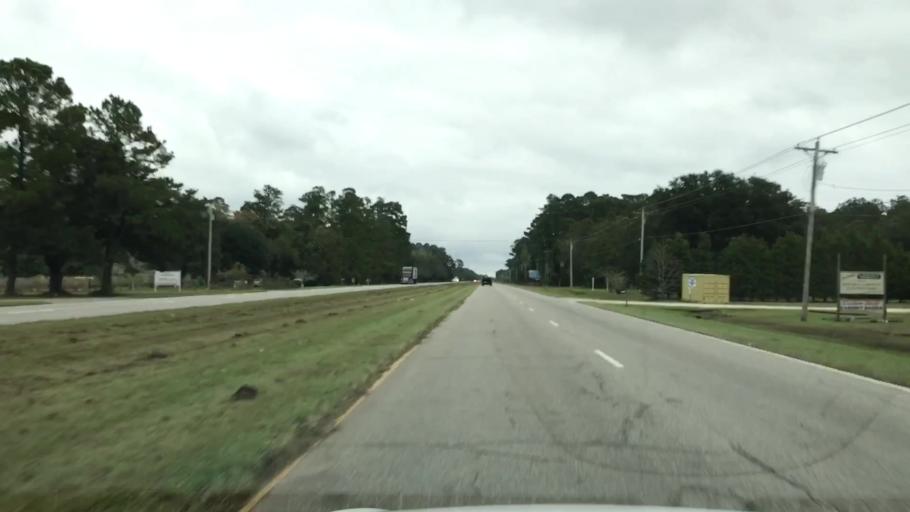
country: US
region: South Carolina
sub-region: Georgetown County
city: Georgetown
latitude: 33.3102
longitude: -79.3319
